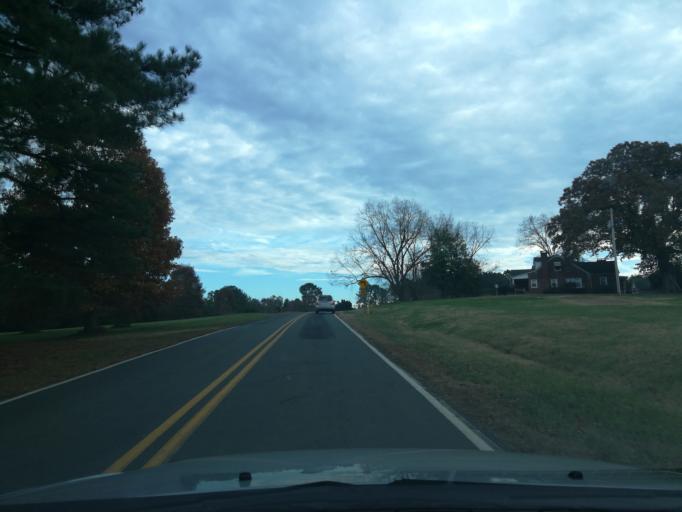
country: US
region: North Carolina
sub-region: Orange County
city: Carrboro
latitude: 35.9791
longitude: -79.0775
